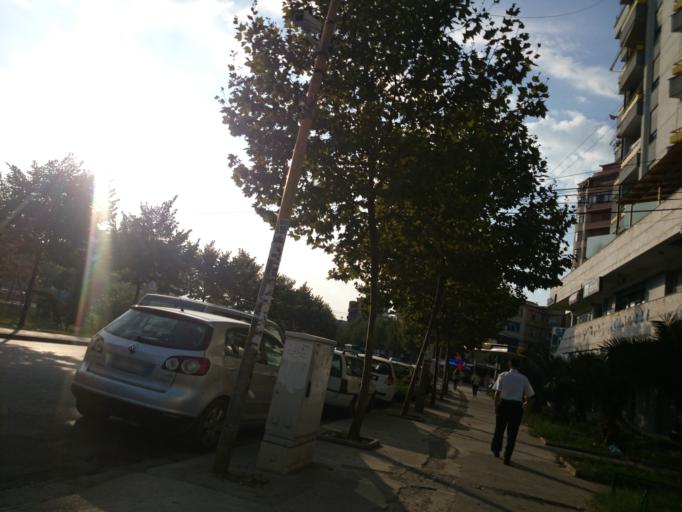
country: AL
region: Tirane
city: Tirana
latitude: 41.3217
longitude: 19.7920
